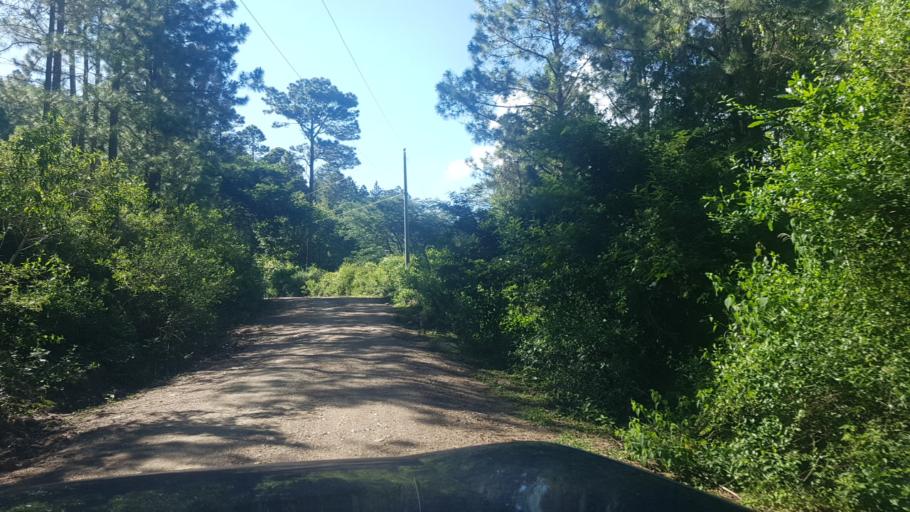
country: NI
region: Nueva Segovia
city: Ocotal
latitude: 13.6415
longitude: -86.6340
